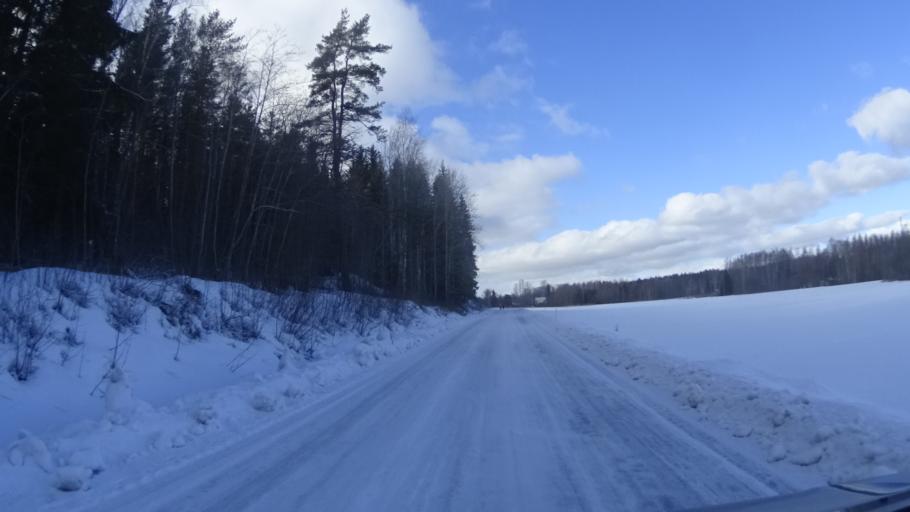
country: FI
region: Uusimaa
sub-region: Helsinki
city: Vantaa
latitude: 60.2466
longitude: 25.1720
